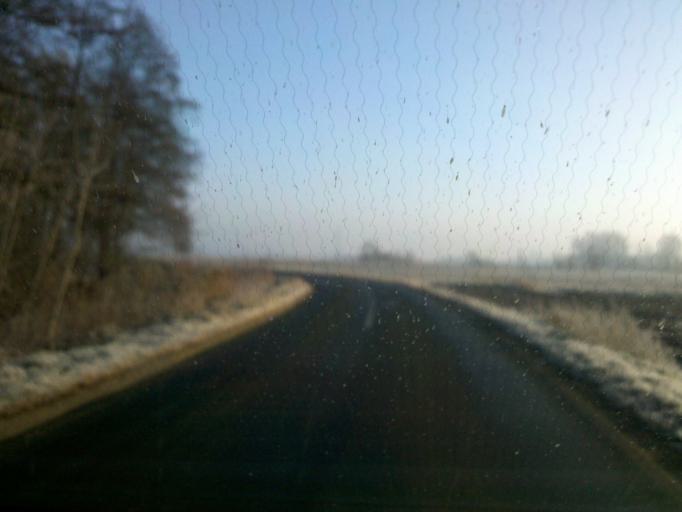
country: HR
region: Medimurska
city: Kotoriba
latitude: 46.2810
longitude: 16.7496
